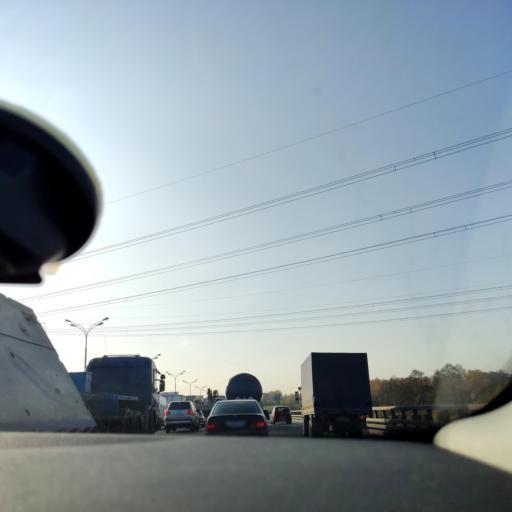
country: RU
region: Moscow
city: Zyablikovo
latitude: 55.6145
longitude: 37.7755
